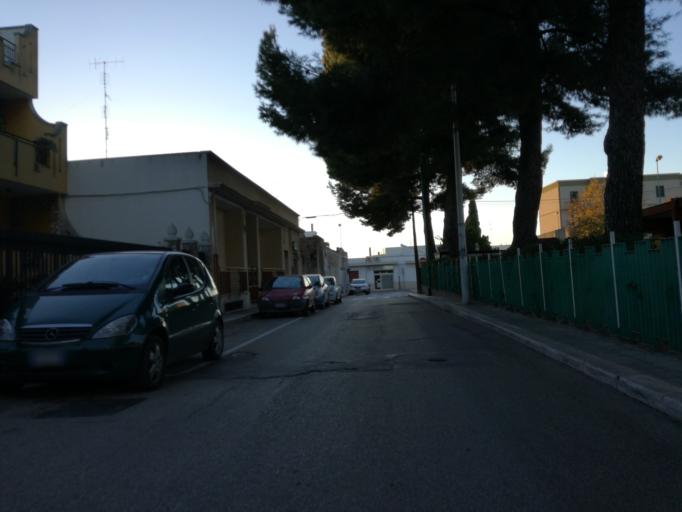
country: IT
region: Apulia
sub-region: Provincia di Bari
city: Adelfia
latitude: 41.0002
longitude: 16.8770
